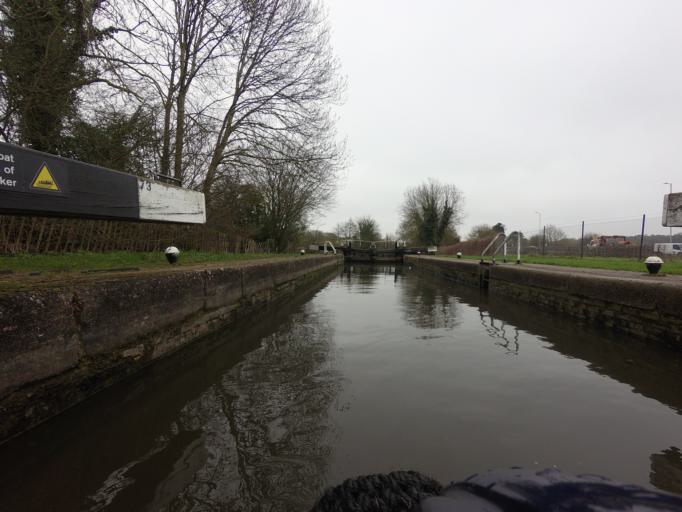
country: GB
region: England
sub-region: Hertfordshire
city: Abbots Langley
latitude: 51.6890
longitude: -0.4340
